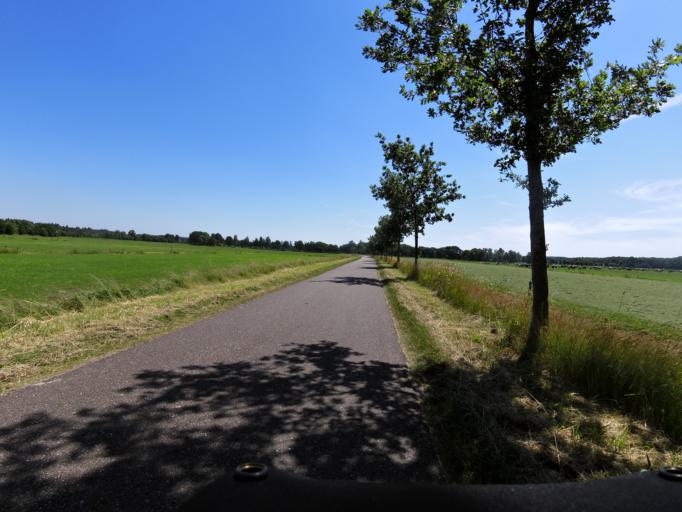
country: NL
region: Overijssel
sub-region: Gemeente Twenterand
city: Den Ham
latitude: 52.5024
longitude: 6.4002
